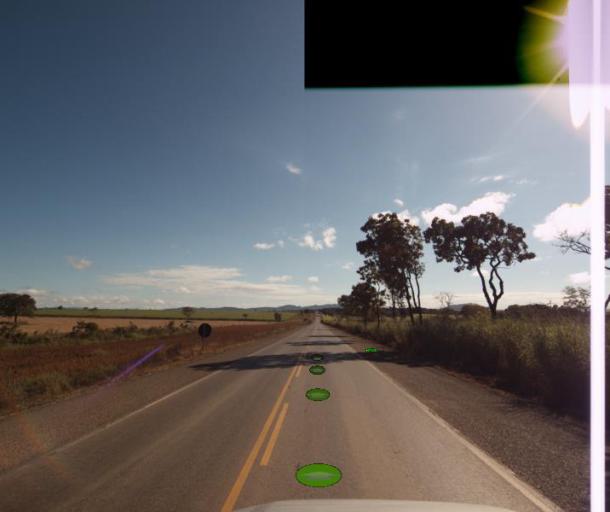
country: BR
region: Goias
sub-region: Uruacu
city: Uruacu
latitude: -14.6604
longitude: -49.1928
